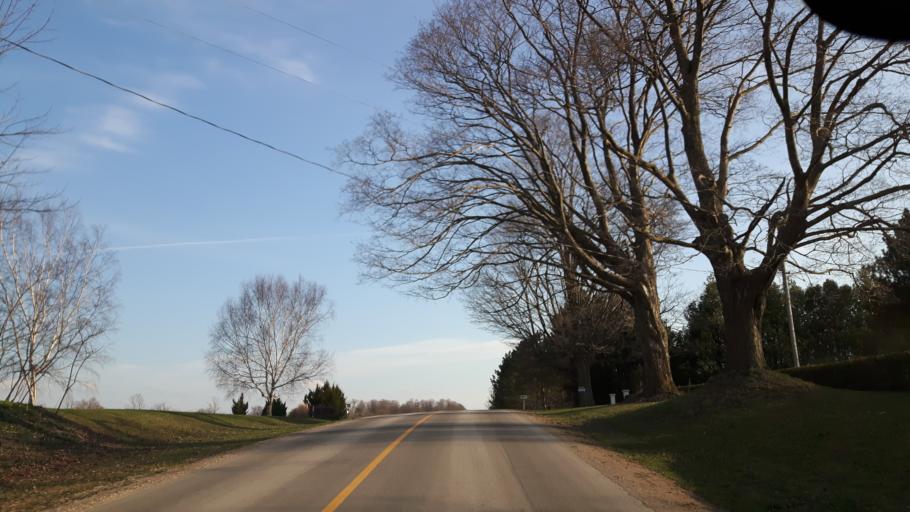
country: CA
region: Ontario
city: Goderich
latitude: 43.6563
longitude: -81.6643
